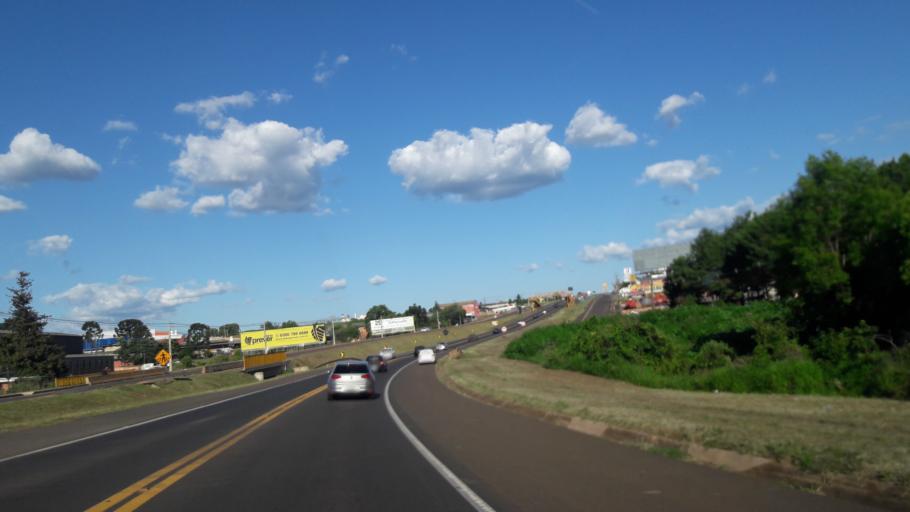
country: BR
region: Parana
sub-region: Guarapuava
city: Guarapuava
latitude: -25.3662
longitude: -51.4917
